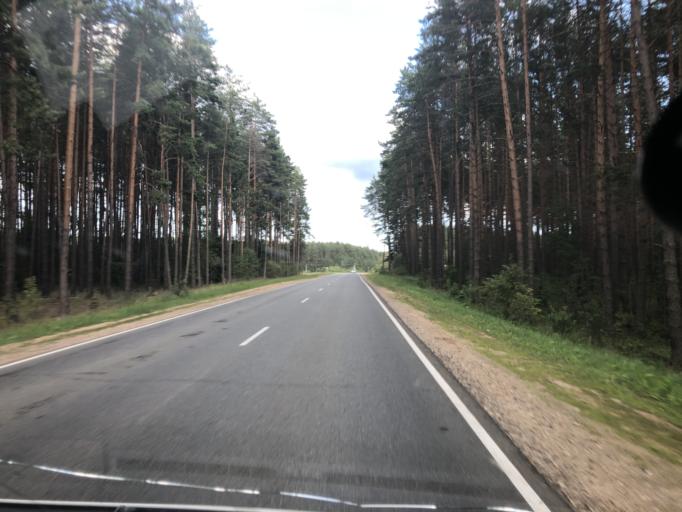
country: RU
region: Kaluga
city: Yukhnov
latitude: 54.7244
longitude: 35.2094
